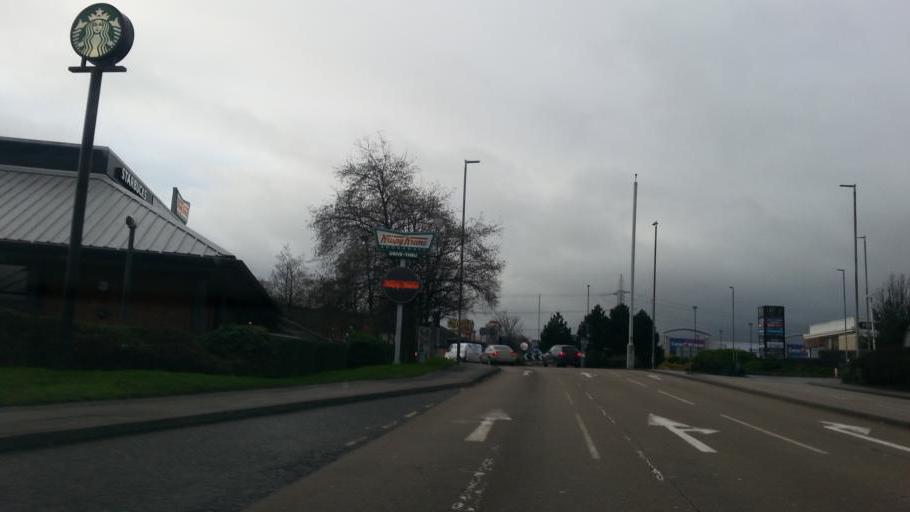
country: GB
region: England
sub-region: City and Borough of Leeds
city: Gildersome
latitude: 53.7445
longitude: -1.6426
